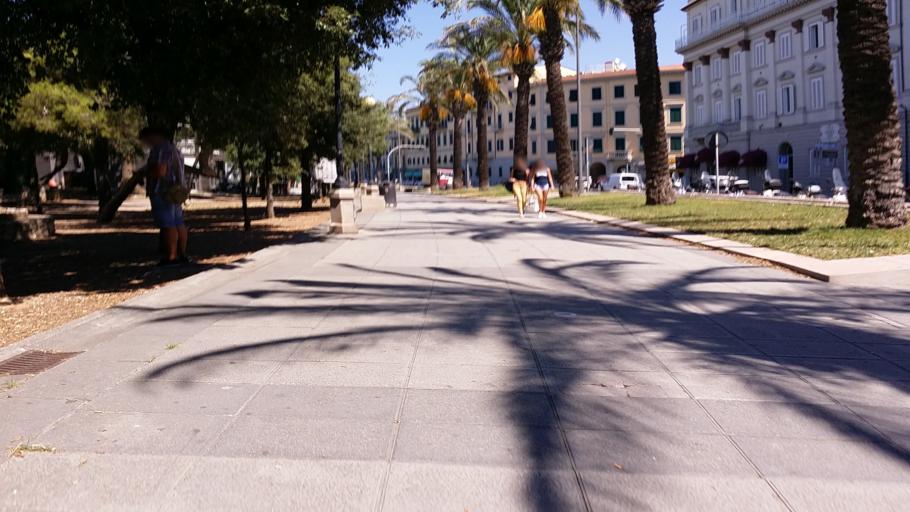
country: IT
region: Tuscany
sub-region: Provincia di Livorno
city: Livorno
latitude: 43.5372
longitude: 10.3018
